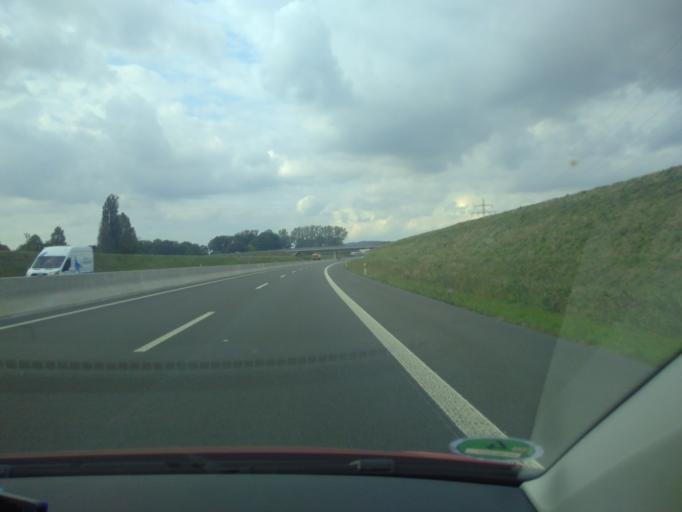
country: DE
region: North Rhine-Westphalia
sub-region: Regierungsbezirk Detmold
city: Steinhagen
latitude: 51.9928
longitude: 8.4449
